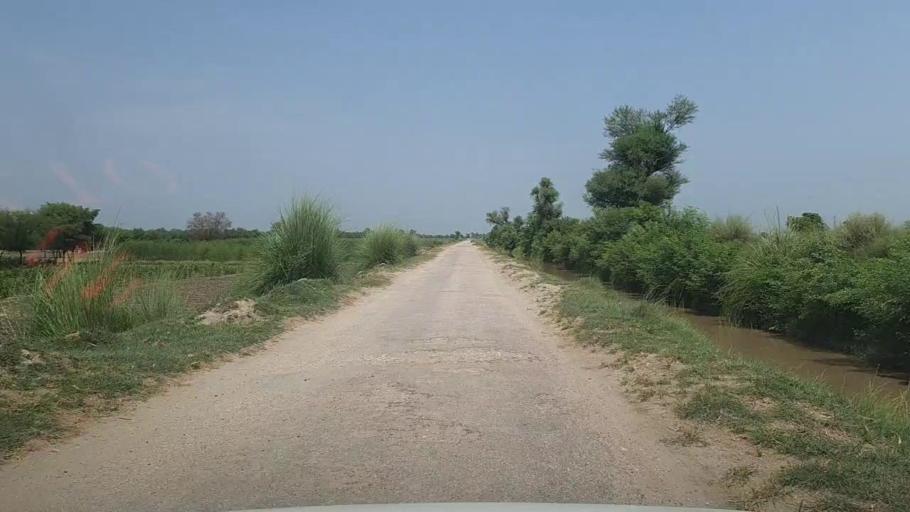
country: PK
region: Sindh
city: Karaundi
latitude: 26.8787
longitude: 68.3355
